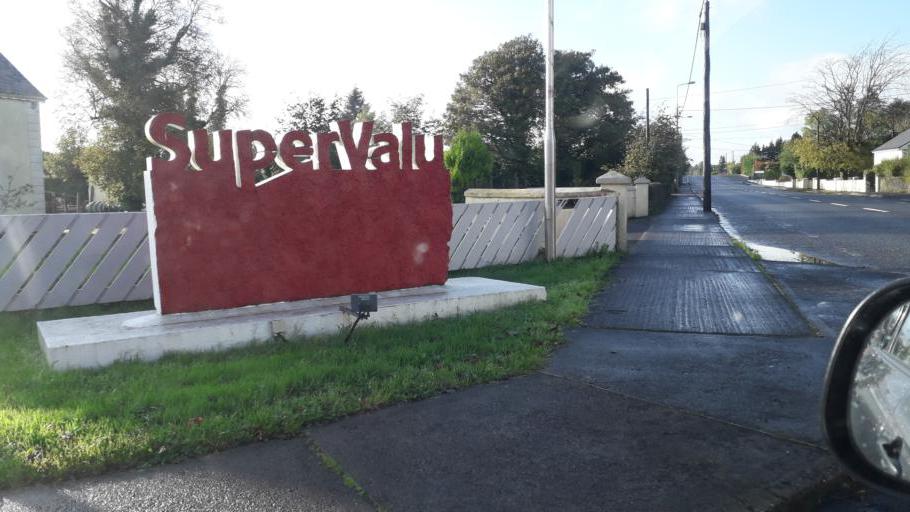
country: IE
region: Connaught
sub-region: Roscommon
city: Ballaghaderreen
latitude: 53.9035
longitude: -8.5838
